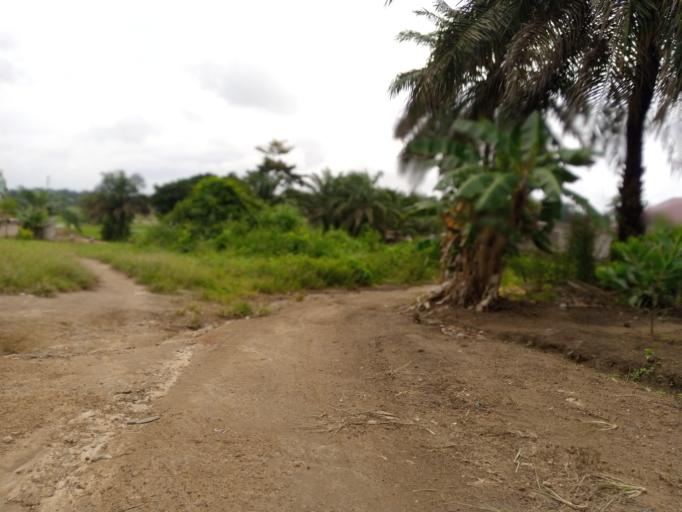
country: SL
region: Eastern Province
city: Kenema
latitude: 7.8797
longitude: -11.1725
